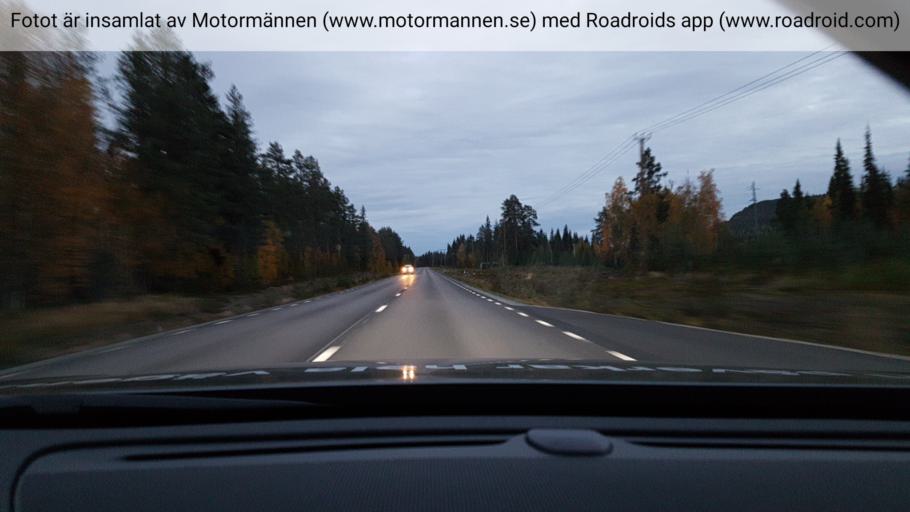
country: SE
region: Norrbotten
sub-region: Alvsbyns Kommun
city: AElvsbyn
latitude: 65.7517
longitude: 20.9067
